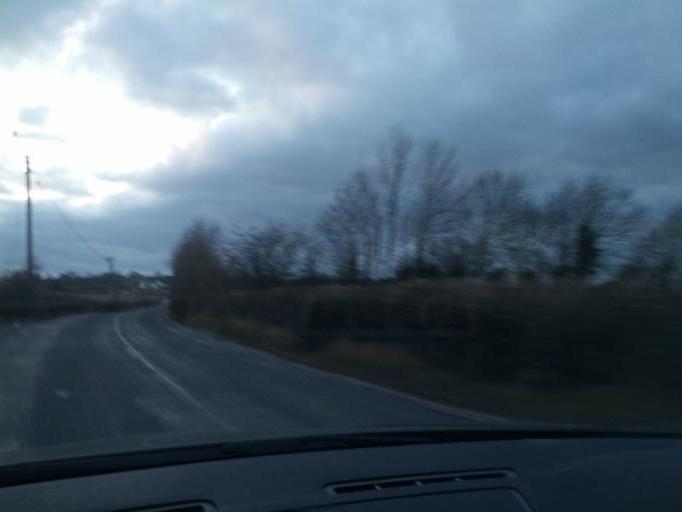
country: IE
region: Connaught
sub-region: County Galway
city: Portumna
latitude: 53.1110
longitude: -8.1061
